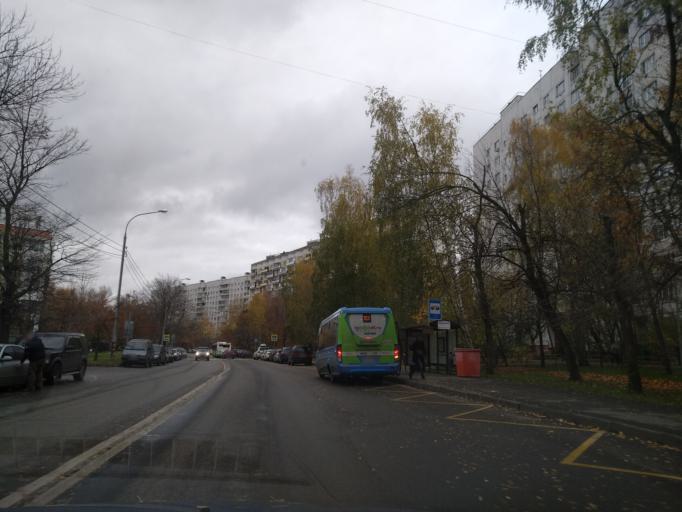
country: RU
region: Moscow
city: Bibirevo
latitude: 55.8935
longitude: 37.6014
